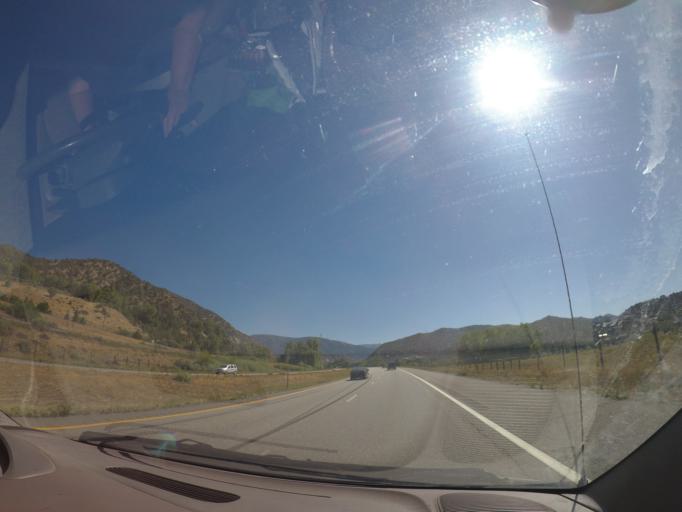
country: US
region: Colorado
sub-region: Garfield County
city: New Castle
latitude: 39.5577
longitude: -107.5595
